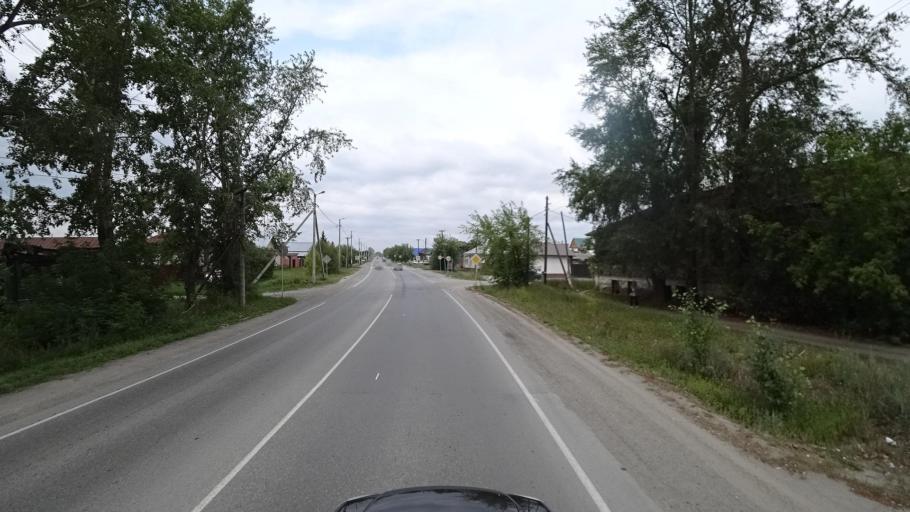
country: RU
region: Sverdlovsk
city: Kamyshlov
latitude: 56.8473
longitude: 62.6738
